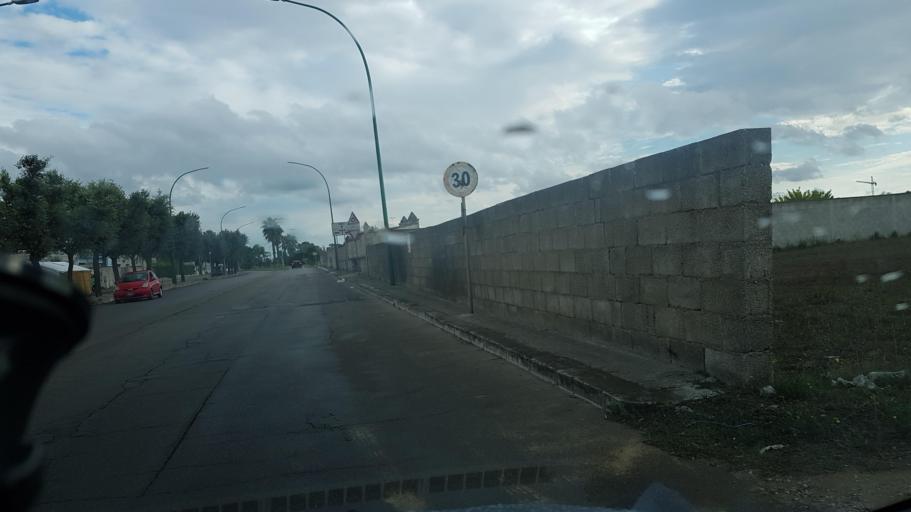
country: IT
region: Apulia
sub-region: Provincia di Lecce
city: Surbo
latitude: 40.3838
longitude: 18.1355
